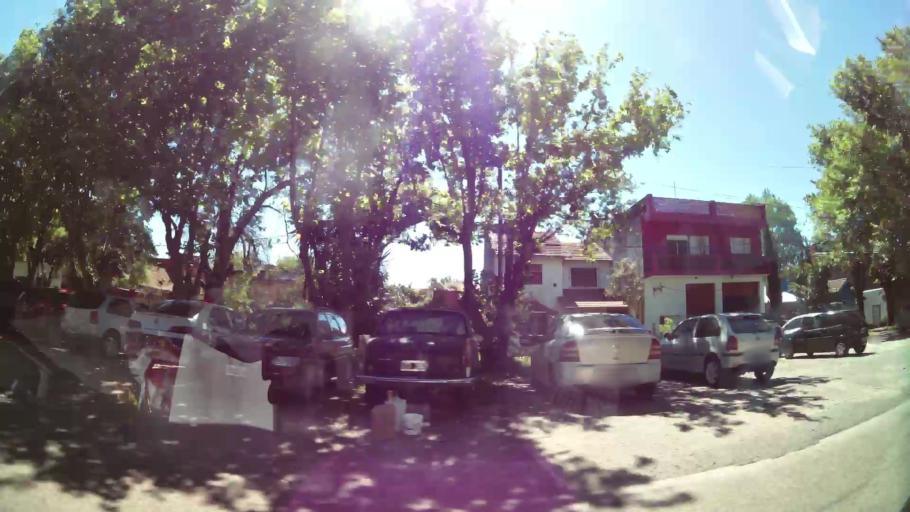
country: AR
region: Buenos Aires
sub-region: Partido de San Isidro
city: San Isidro
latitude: -34.4630
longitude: -58.5076
